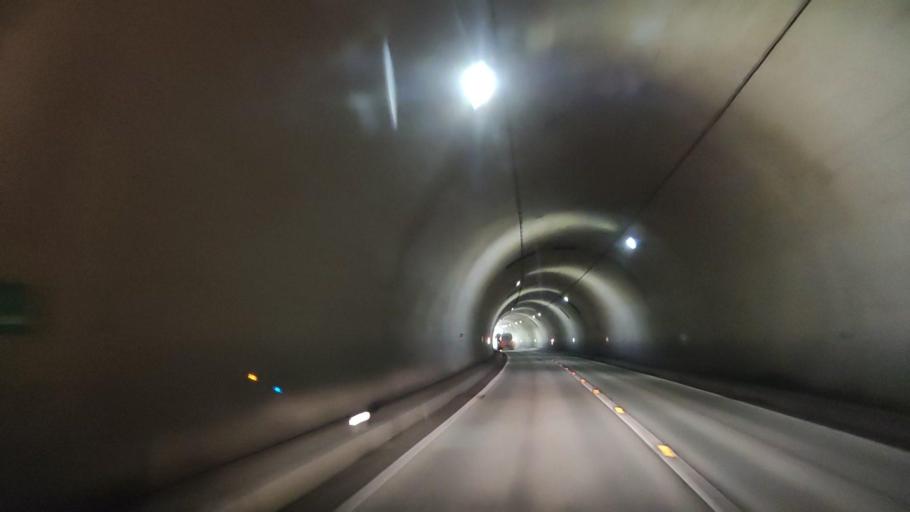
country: JP
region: Tottori
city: Yonago
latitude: 35.2629
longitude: 133.4360
